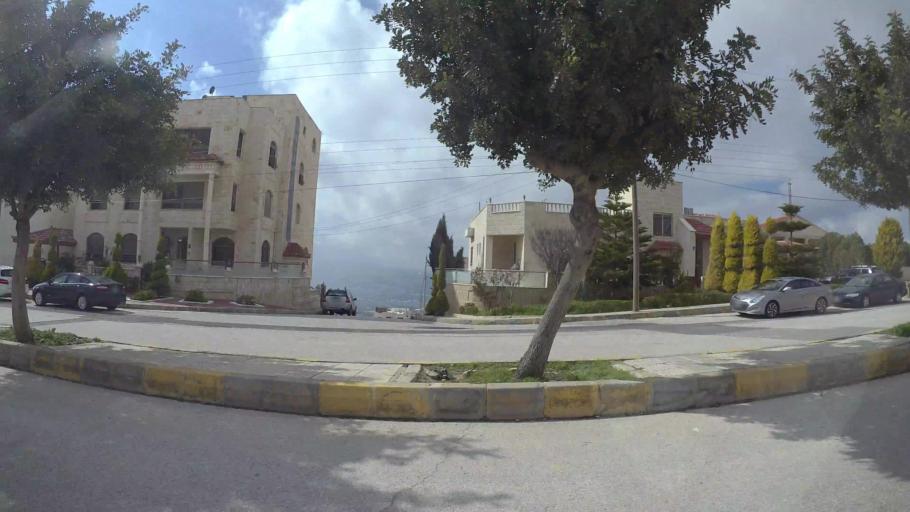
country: JO
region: Amman
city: Al Jubayhah
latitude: 32.0733
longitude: 35.8819
